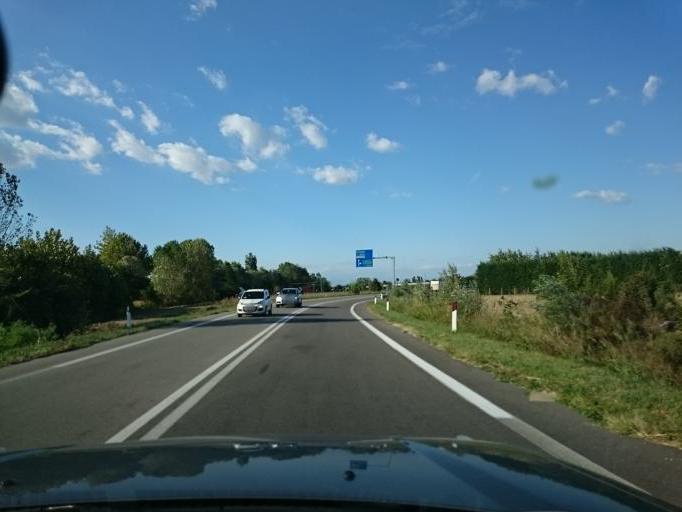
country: IT
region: Veneto
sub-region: Provincia di Padova
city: Tencarola
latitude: 45.3777
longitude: 11.8255
